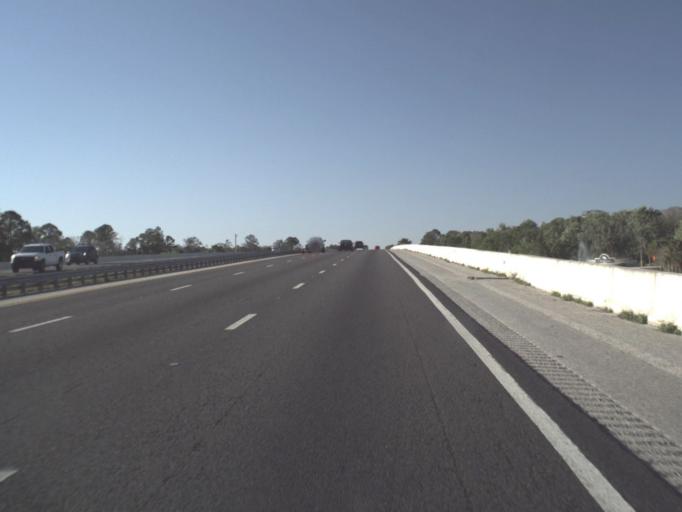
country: US
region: Florida
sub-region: Flagler County
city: Flagler Beach
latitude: 29.4732
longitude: -81.1826
